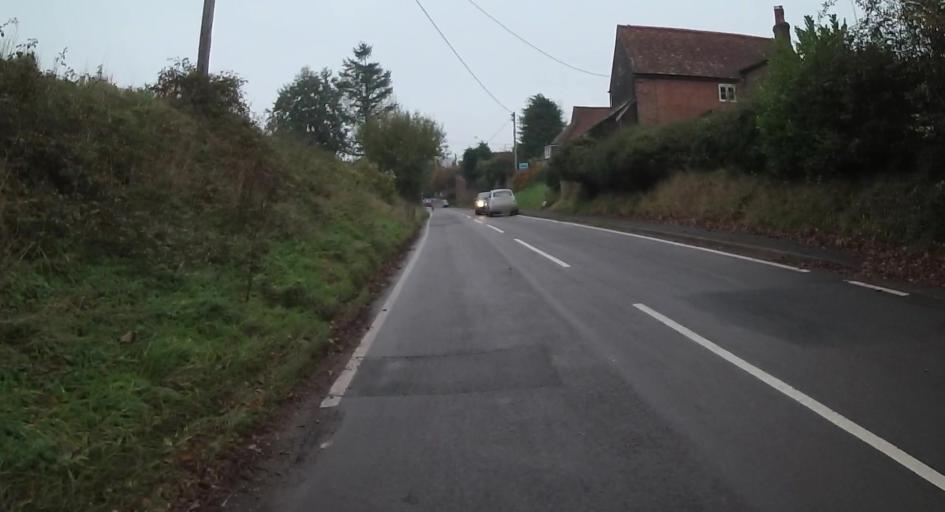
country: GB
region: England
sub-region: Hampshire
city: Kingsley
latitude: 51.1639
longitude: -0.8981
